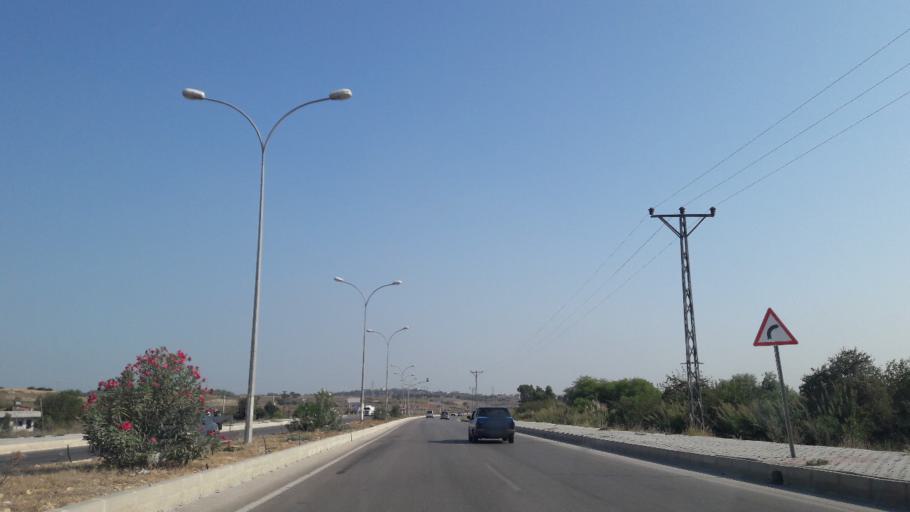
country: TR
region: Adana
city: Yuregir
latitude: 37.0592
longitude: 35.4440
